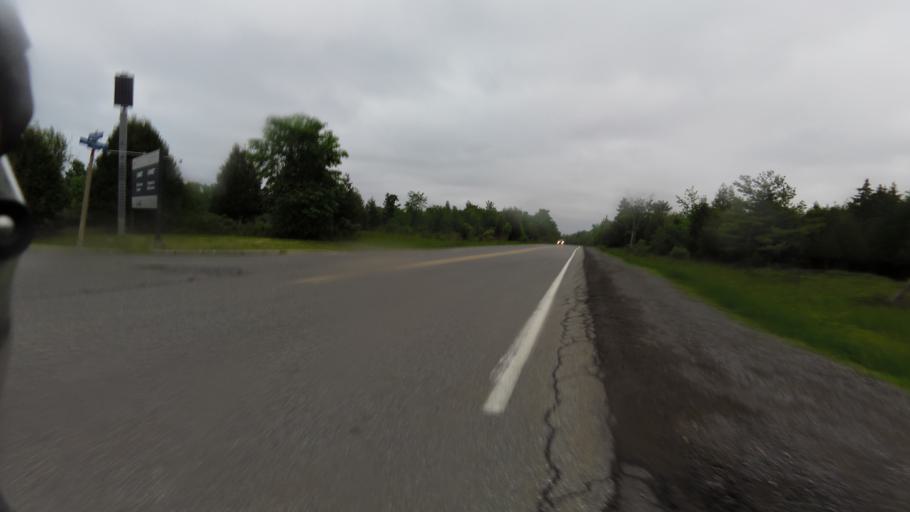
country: CA
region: Ontario
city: Bells Corners
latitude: 45.3168
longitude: -75.8623
